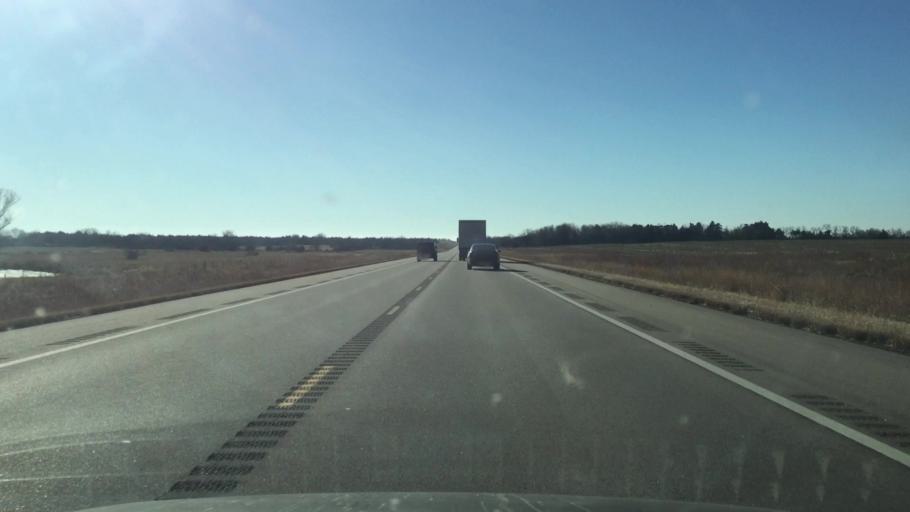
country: US
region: Kansas
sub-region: Allen County
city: Iola
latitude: 38.0439
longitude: -95.3806
